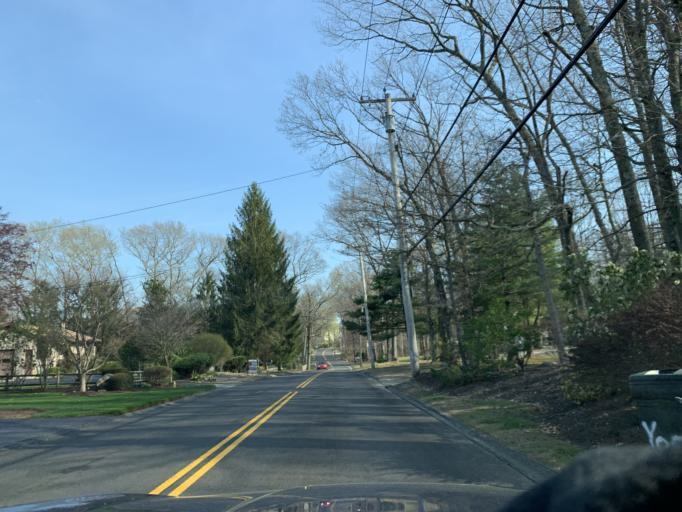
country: US
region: Rhode Island
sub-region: Providence County
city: Johnston
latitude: 41.7656
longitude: -71.4991
